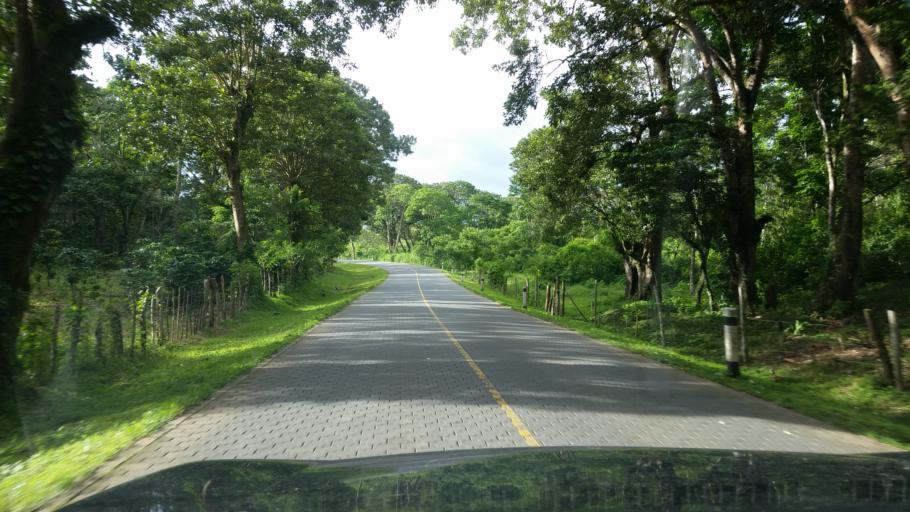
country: NI
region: Matagalpa
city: San Ramon
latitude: 13.1696
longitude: -85.7275
